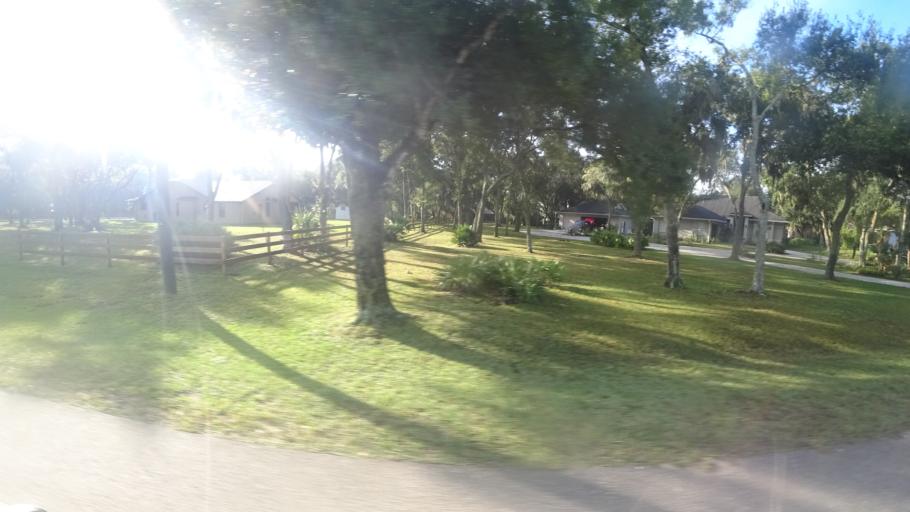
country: US
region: Florida
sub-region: Manatee County
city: Ellenton
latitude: 27.5425
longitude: -82.4565
